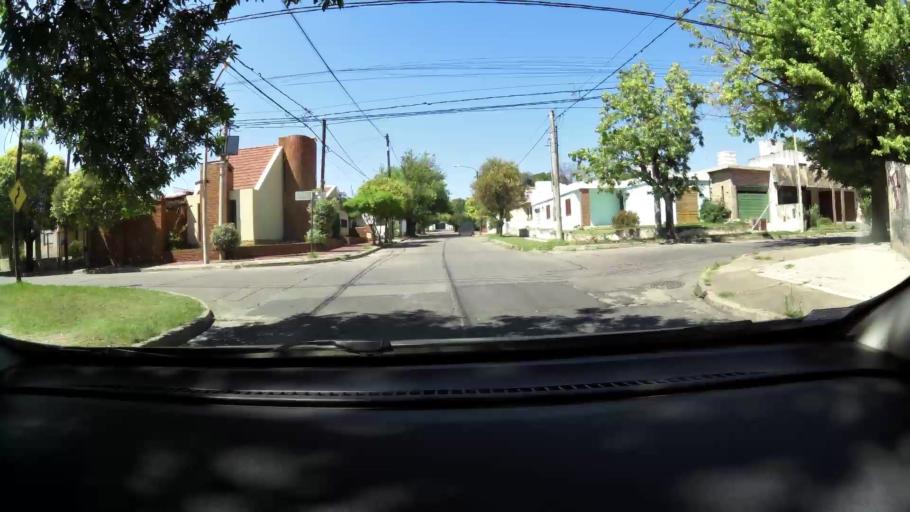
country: AR
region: Cordoba
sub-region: Departamento de Capital
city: Cordoba
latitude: -31.4179
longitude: -64.2132
